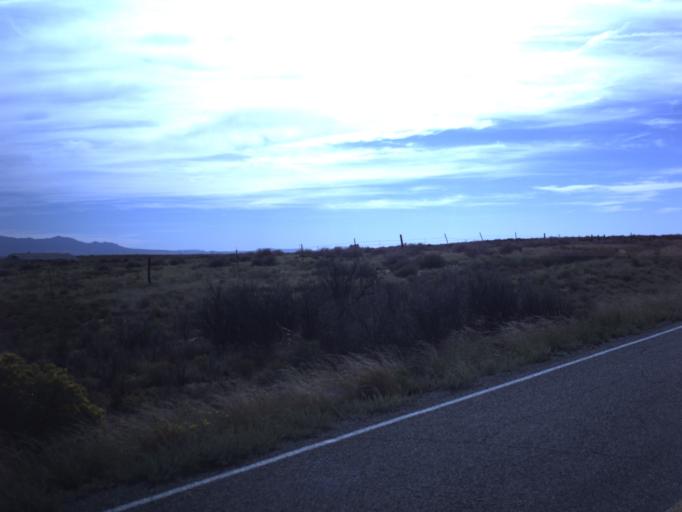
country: US
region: Utah
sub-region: San Juan County
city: Blanding
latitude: 37.3314
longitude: -109.3458
